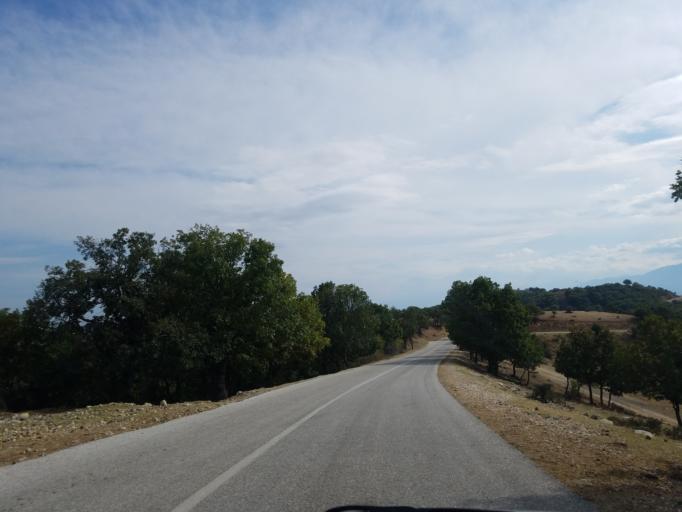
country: GR
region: Thessaly
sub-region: Trikala
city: Kastraki
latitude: 39.7591
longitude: 21.6636
